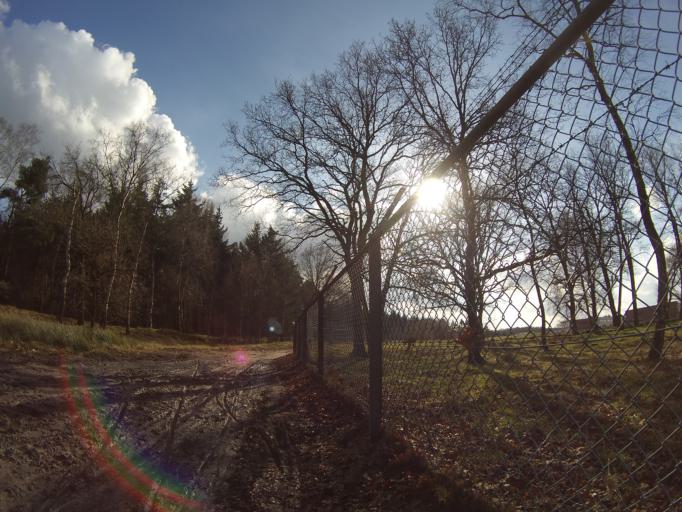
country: NL
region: Utrecht
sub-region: Gemeente Soest
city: Soest
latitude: 52.1432
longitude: 5.2569
